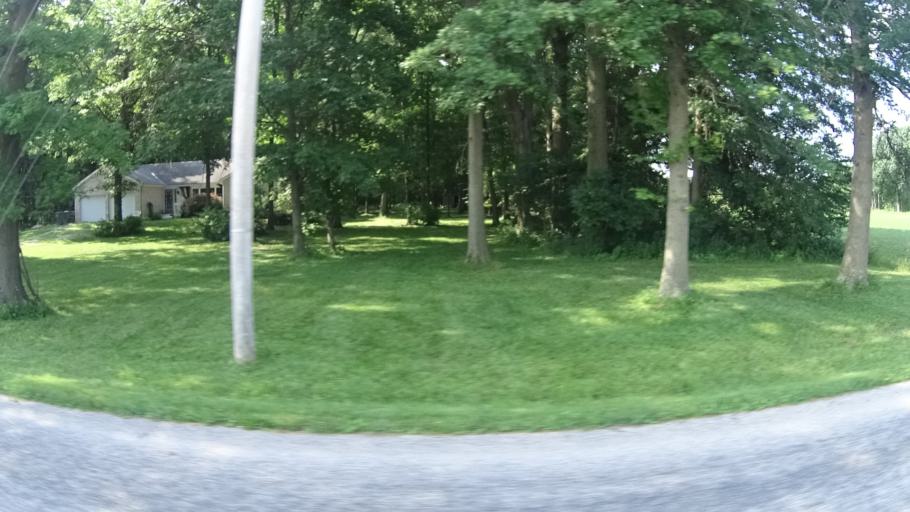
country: US
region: Ohio
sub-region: Lorain County
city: Vermilion
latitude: 41.3761
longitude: -82.4351
